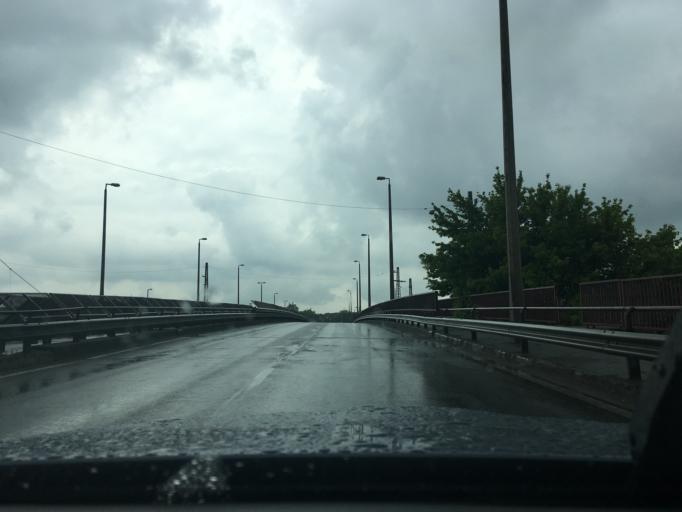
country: HU
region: Hajdu-Bihar
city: Debrecen
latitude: 47.5203
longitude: 21.6323
